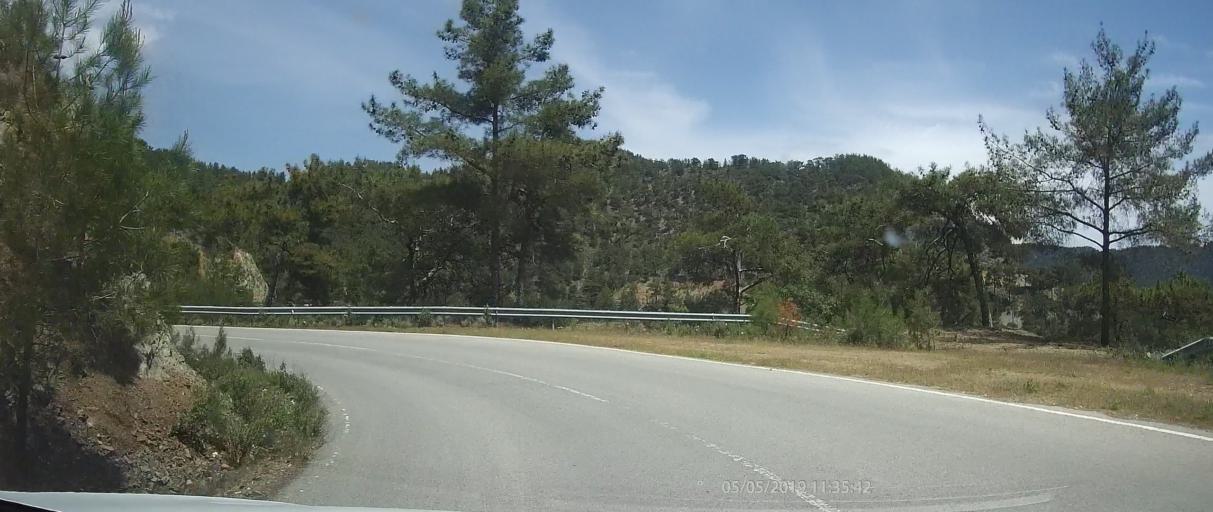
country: CY
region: Lefkosia
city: Kato Pyrgos
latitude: 34.9696
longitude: 32.6518
